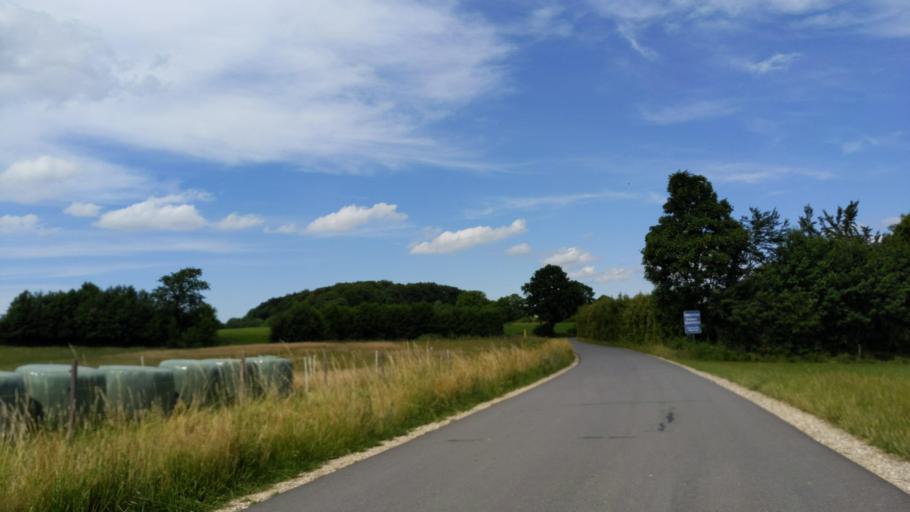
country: DE
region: Schleswig-Holstein
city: Kasseedorf
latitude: 54.1204
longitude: 10.7080
